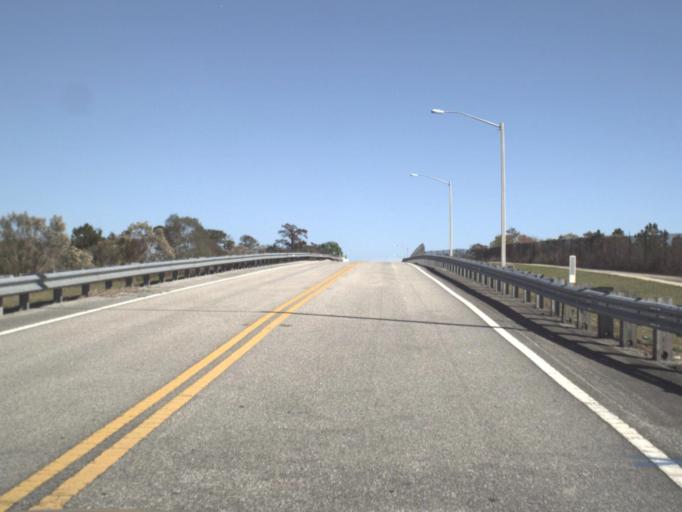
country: US
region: Florida
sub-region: Flagler County
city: Palm Coast
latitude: 29.5990
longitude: -81.2499
